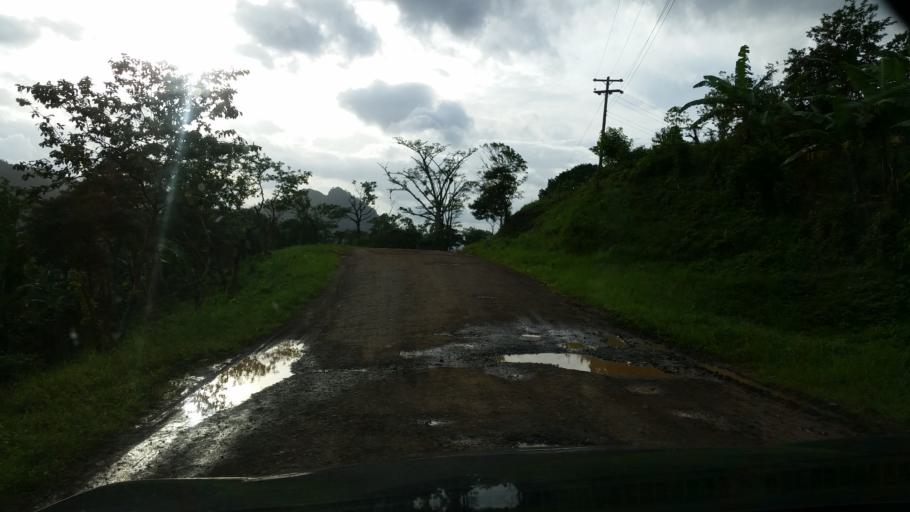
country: NI
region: Jinotega
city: Jinotega
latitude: 13.2683
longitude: -85.7304
